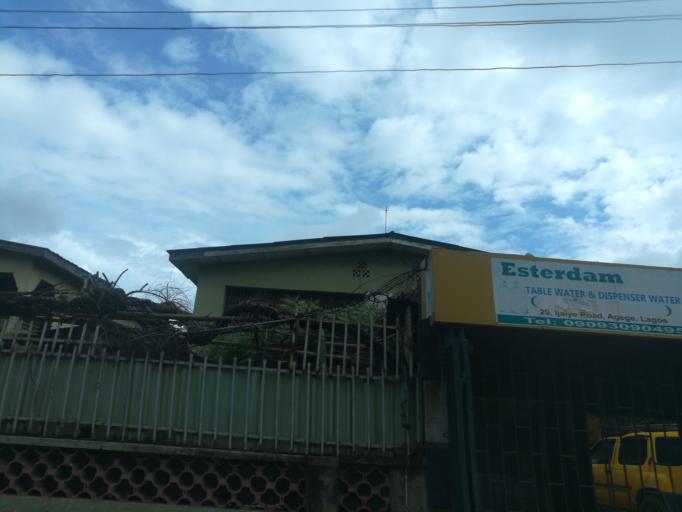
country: NG
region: Lagos
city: Agege
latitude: 6.6253
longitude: 3.3332
